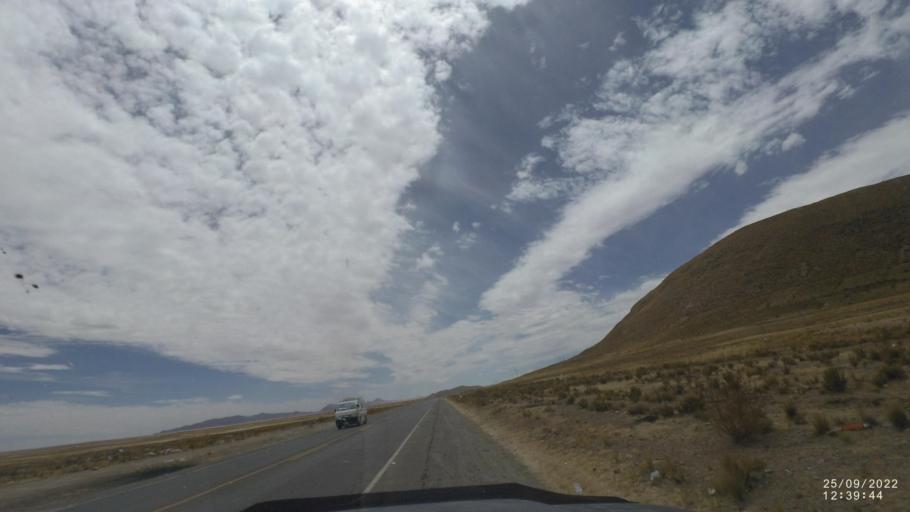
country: BO
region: Oruro
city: Machacamarca
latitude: -18.1233
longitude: -67.0050
